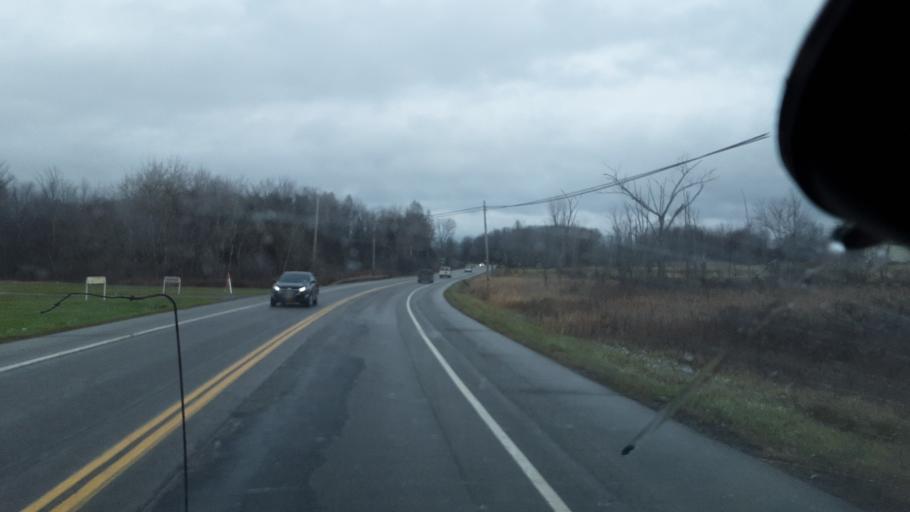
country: US
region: New York
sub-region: Cattaraugus County
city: Delevan
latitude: 42.5084
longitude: -78.4796
